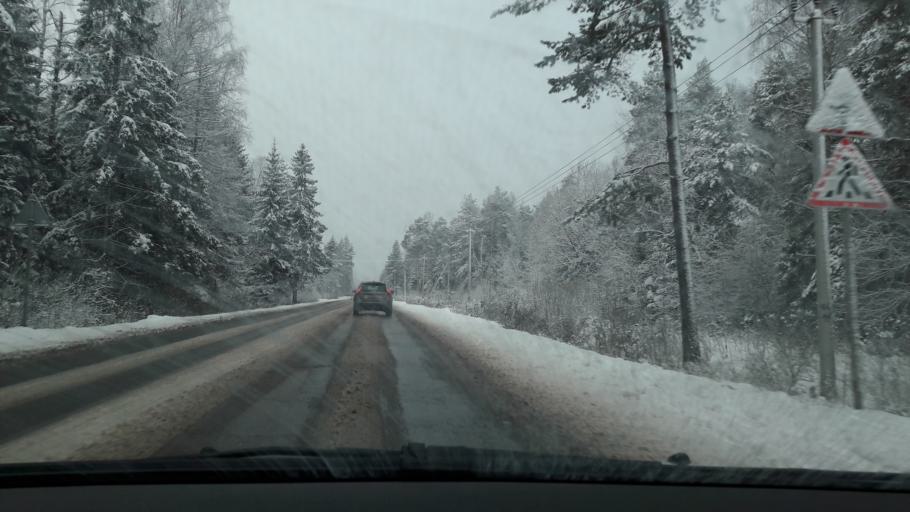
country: RU
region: Moskovskaya
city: Zvenigorod
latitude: 55.6393
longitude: 36.8453
